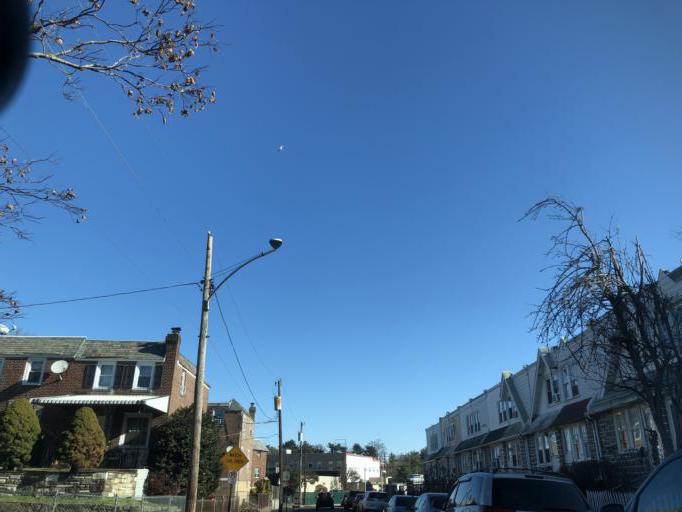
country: US
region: Pennsylvania
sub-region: Delaware County
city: East Lansdowne
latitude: 39.9541
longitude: -75.2602
